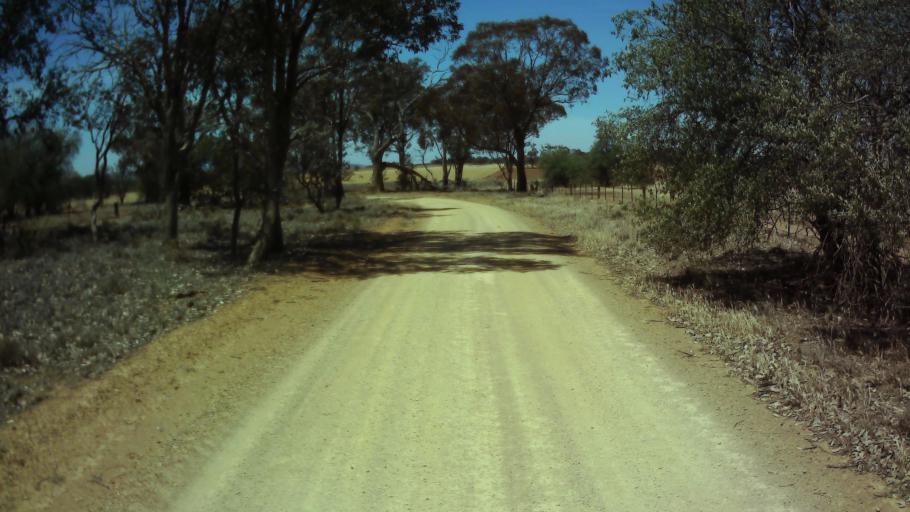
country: AU
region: New South Wales
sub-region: Weddin
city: Grenfell
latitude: -33.9284
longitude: 148.1776
